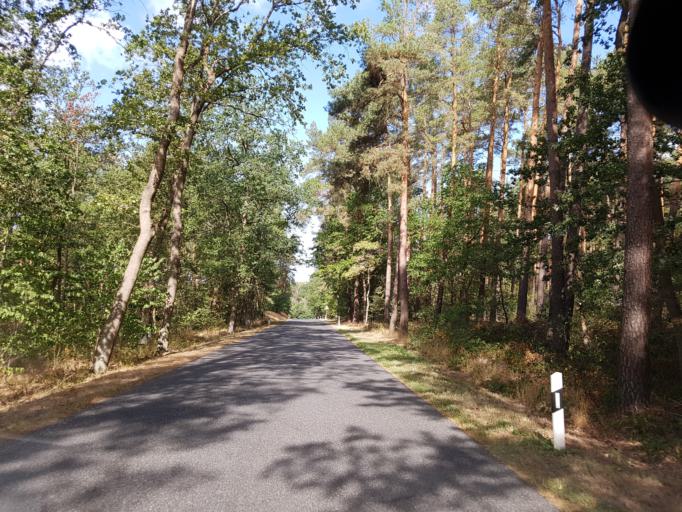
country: DE
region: Brandenburg
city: Sonnewalde
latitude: 51.7393
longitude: 13.6217
